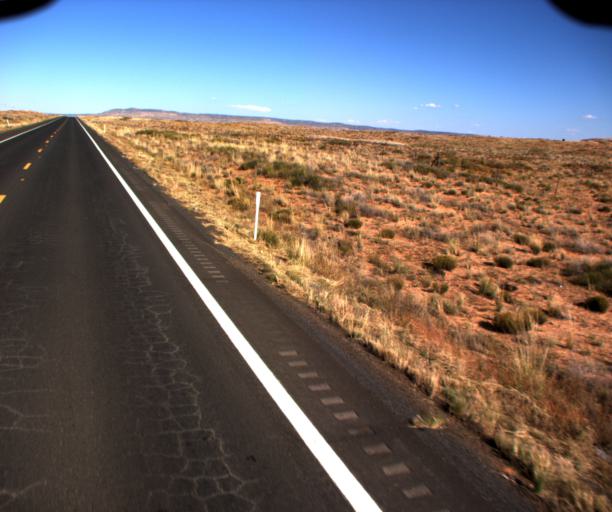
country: US
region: Arizona
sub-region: Coconino County
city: Tuba City
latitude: 36.2916
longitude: -110.9903
